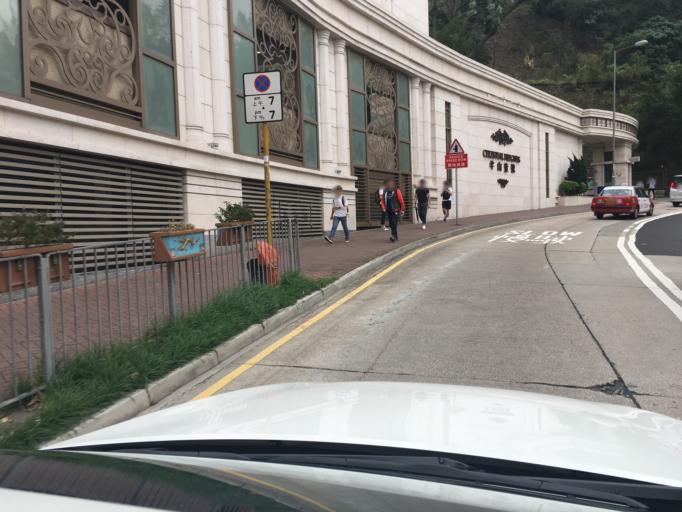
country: HK
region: Kowloon City
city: Kowloon
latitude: 22.3196
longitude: 114.1852
